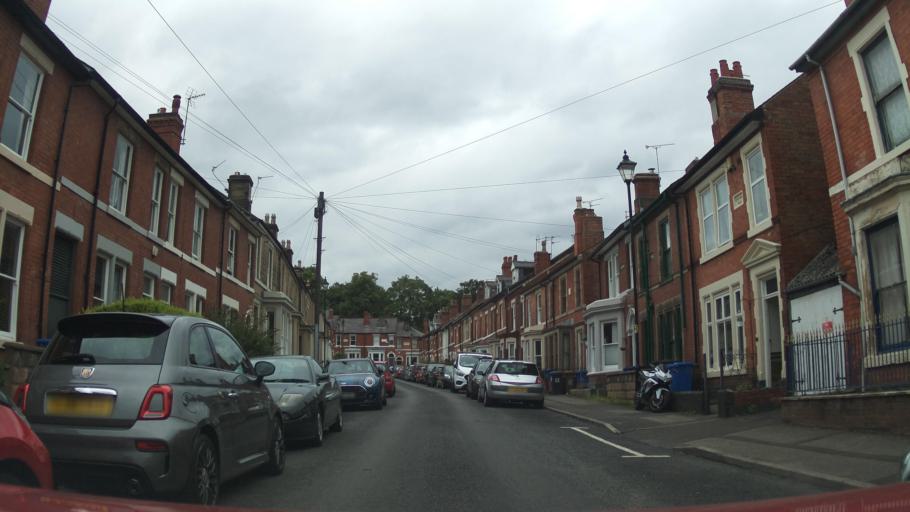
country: GB
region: England
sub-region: Derby
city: Derby
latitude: 52.9313
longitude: -1.4795
